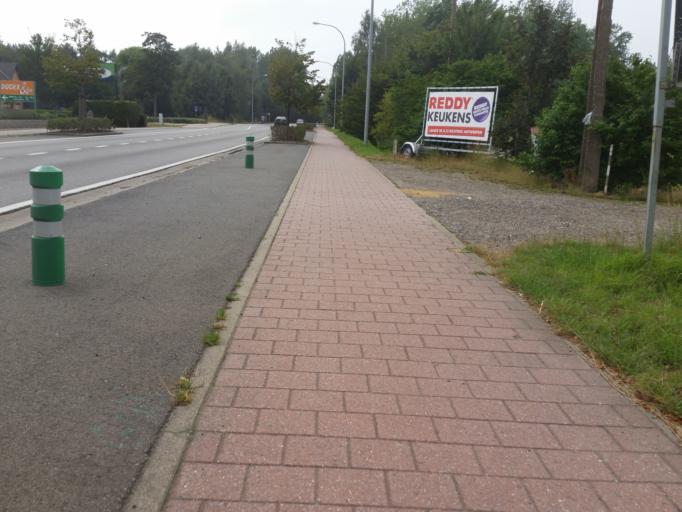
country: BE
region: Flanders
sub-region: Provincie Antwerpen
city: Rumst
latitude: 51.0424
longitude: 4.4318
